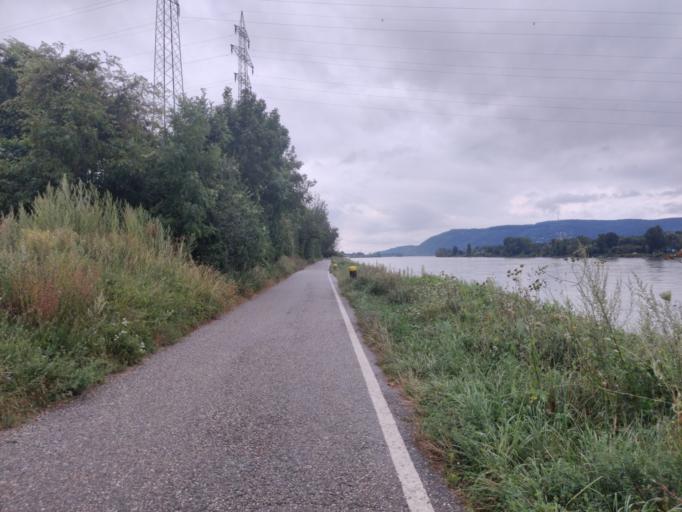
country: AT
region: Lower Austria
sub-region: Politischer Bezirk Korneuburg
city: Bisamberg
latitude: 48.3260
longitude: 16.3351
